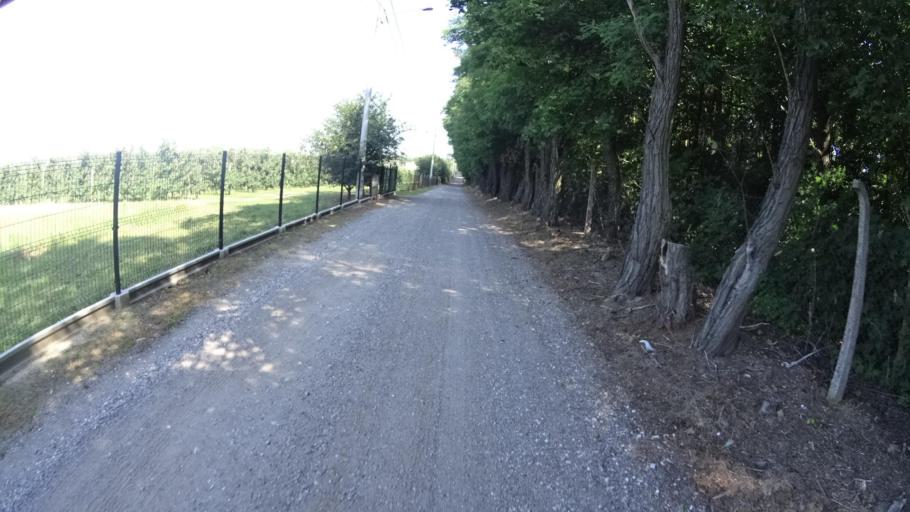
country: PL
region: Masovian Voivodeship
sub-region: Powiat grojecki
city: Grojec
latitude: 51.8474
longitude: 20.8575
